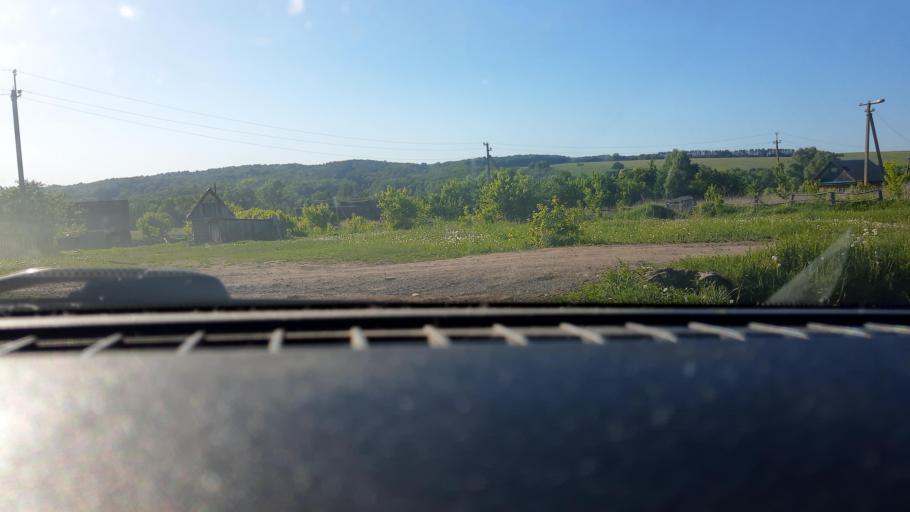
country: RU
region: Bashkortostan
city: Ulukulevo
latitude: 54.5533
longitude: 56.3234
